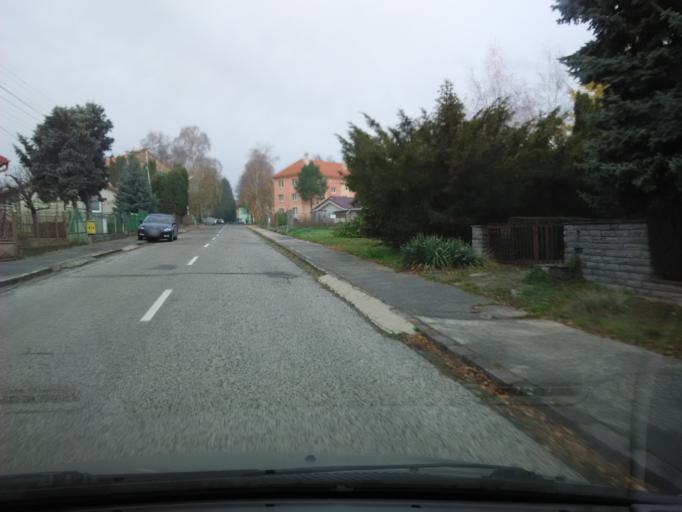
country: SK
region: Nitriansky
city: Tlmace
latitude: 48.2925
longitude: 18.5176
